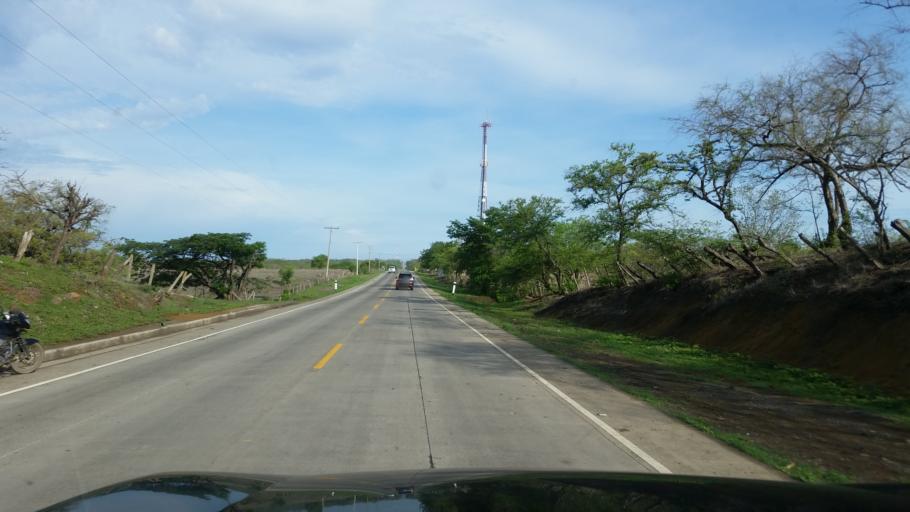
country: NI
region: Leon
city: Nagarote
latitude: 12.1104
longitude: -86.5981
